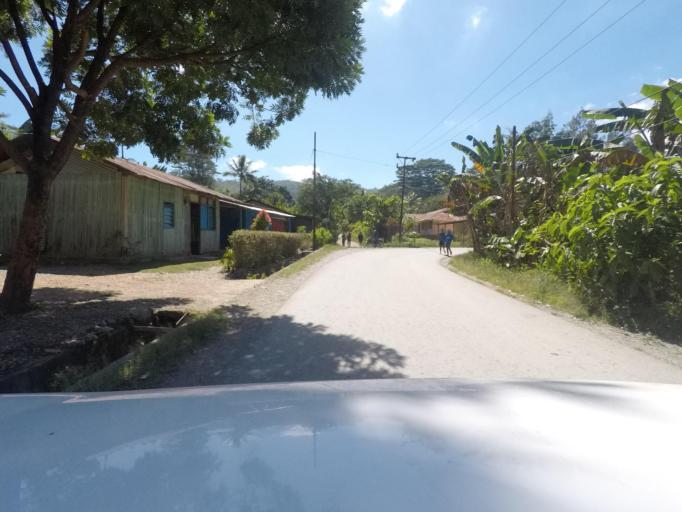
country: TL
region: Ermera
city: Gleno
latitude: -8.7116
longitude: 125.4466
